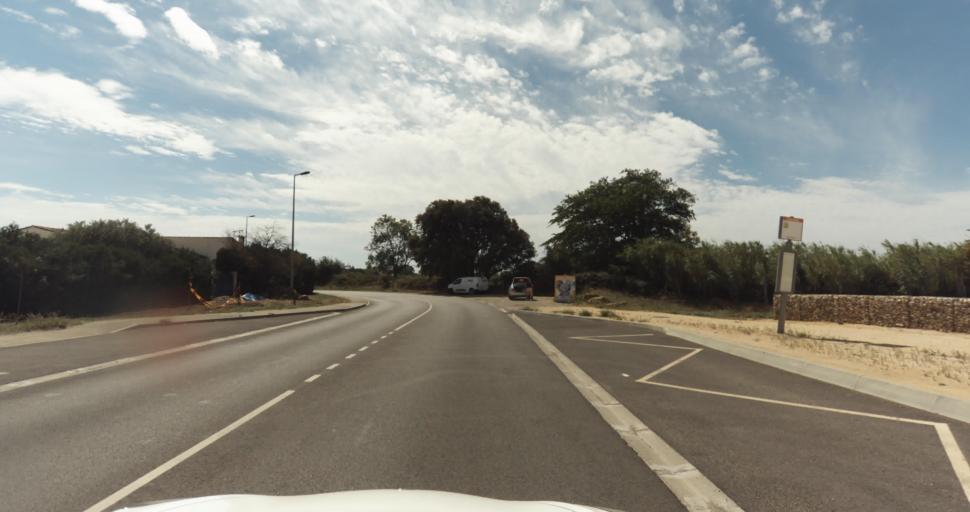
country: FR
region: Provence-Alpes-Cote d'Azur
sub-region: Departement des Bouches-du-Rhone
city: Miramas
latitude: 43.5879
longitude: 4.9940
